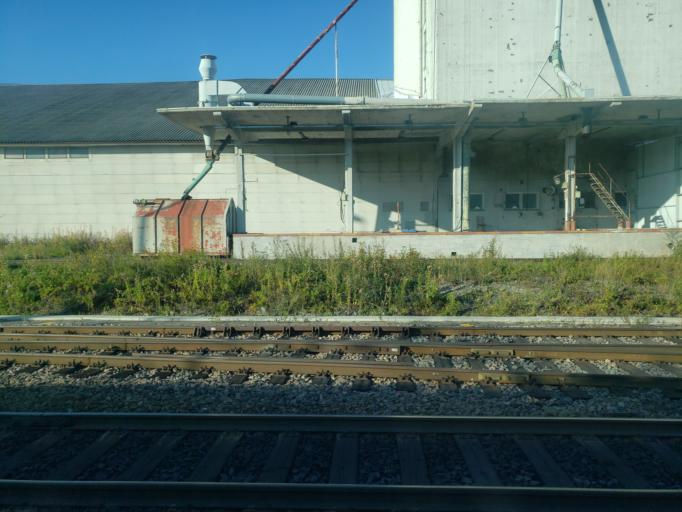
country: FI
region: South Karelia
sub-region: Lappeenranta
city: Lappeenranta
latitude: 60.8654
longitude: 28.2968
